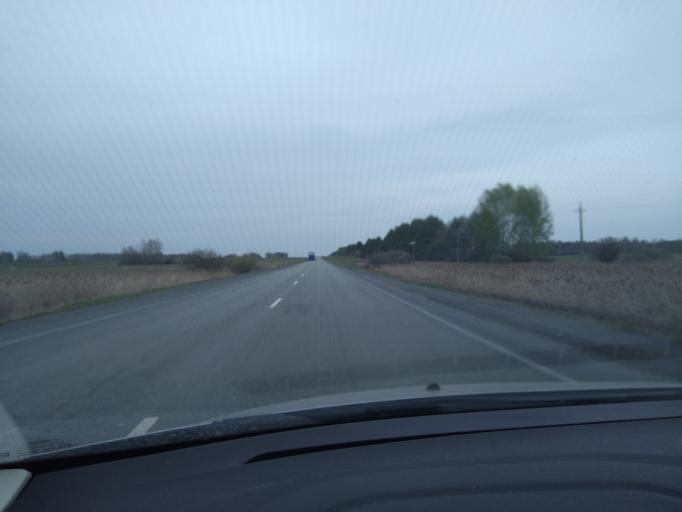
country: RU
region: Sverdlovsk
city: Talitsa
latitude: 57.0643
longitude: 63.5597
